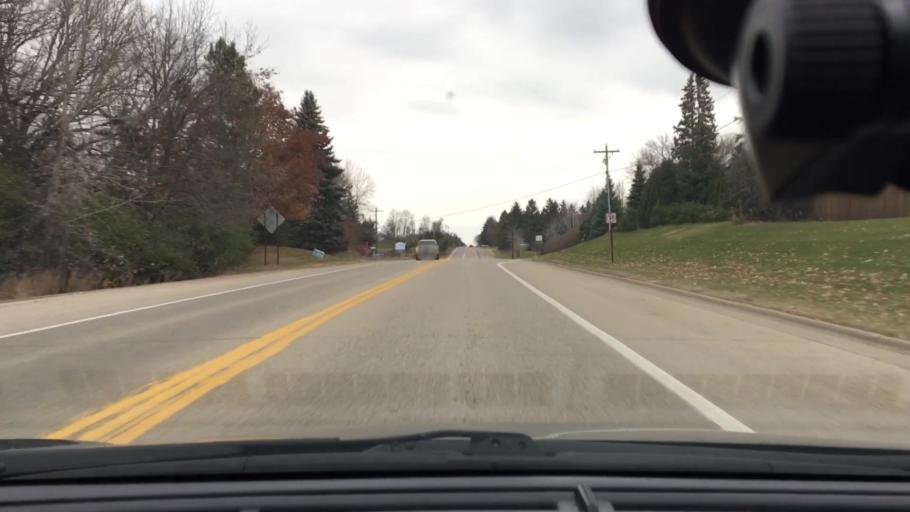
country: US
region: Minnesota
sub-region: Hennepin County
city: Corcoran
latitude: 45.0674
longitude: -93.5221
